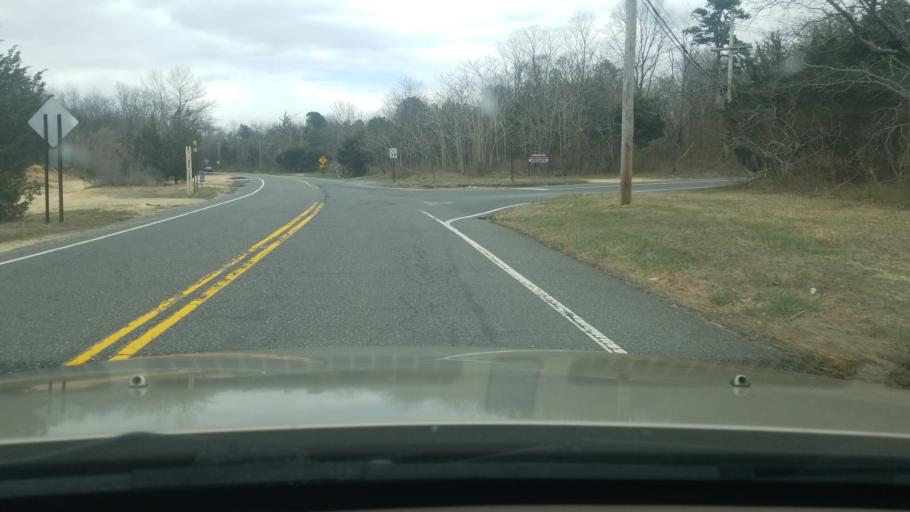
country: US
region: New Jersey
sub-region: Monmouth County
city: Ramtown
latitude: 40.1318
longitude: -74.1173
